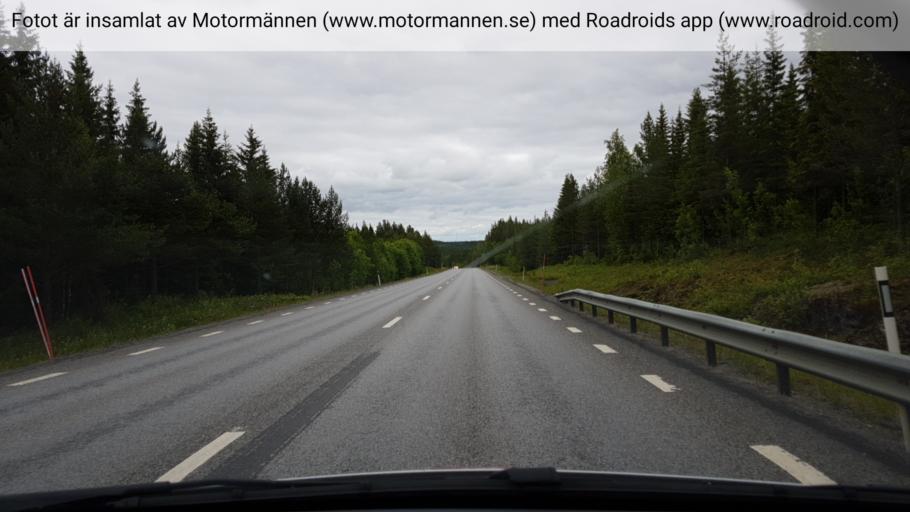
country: SE
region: Jaemtland
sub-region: Are Kommun
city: Jarpen
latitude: 63.3132
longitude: 13.7269
